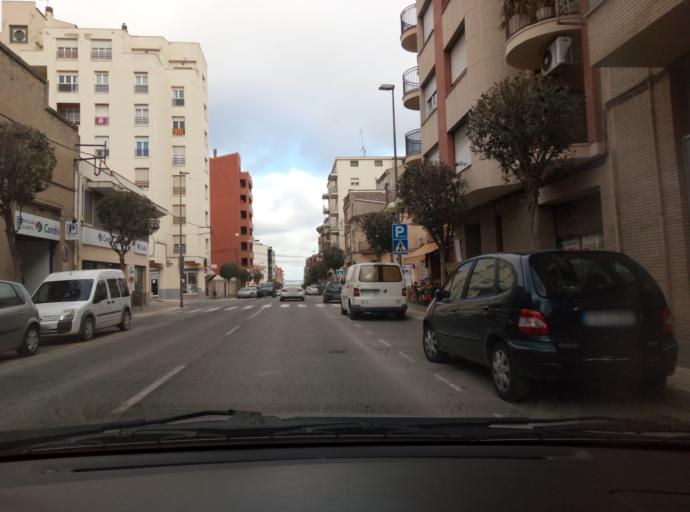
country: ES
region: Catalonia
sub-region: Provincia de Lleida
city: Tarrega
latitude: 41.6526
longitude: 1.1386
